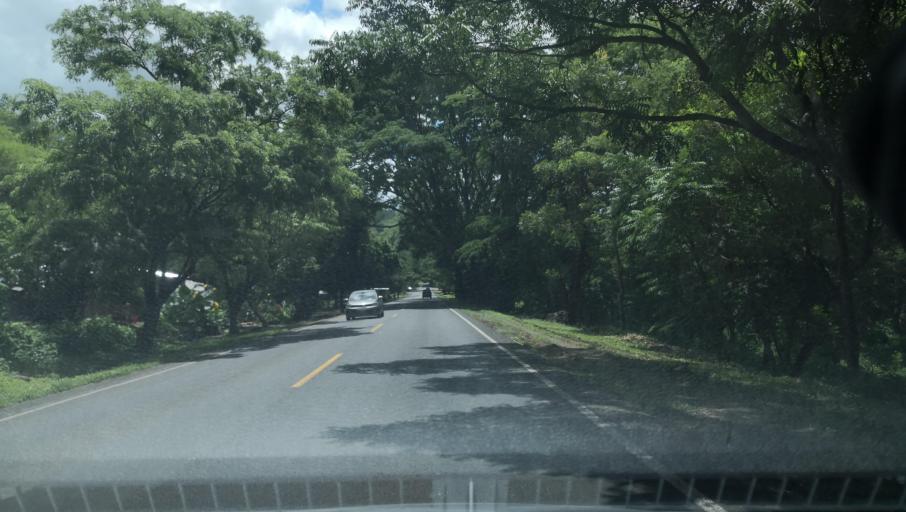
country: NI
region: Esteli
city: Condega
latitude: 13.2962
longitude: -86.3486
